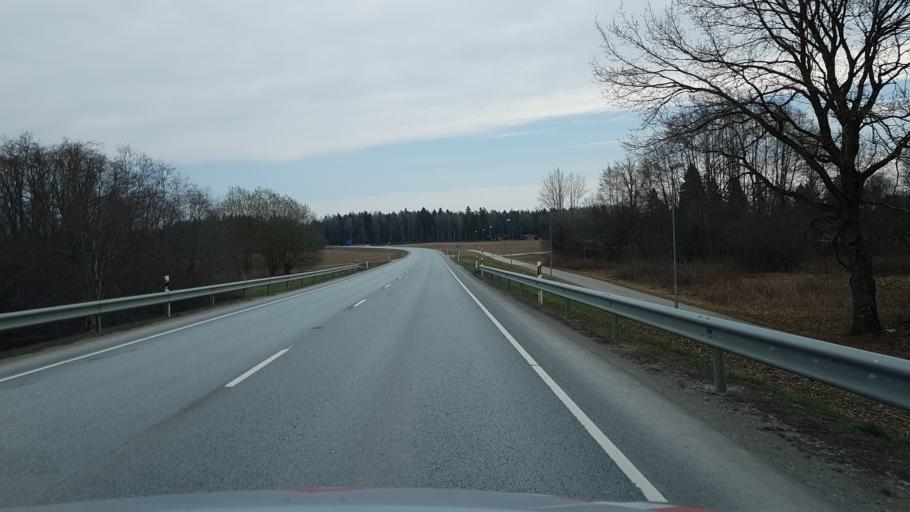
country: EE
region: Laeaene-Virumaa
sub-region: Rakvere linn
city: Rakvere
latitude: 59.3232
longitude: 26.3570
